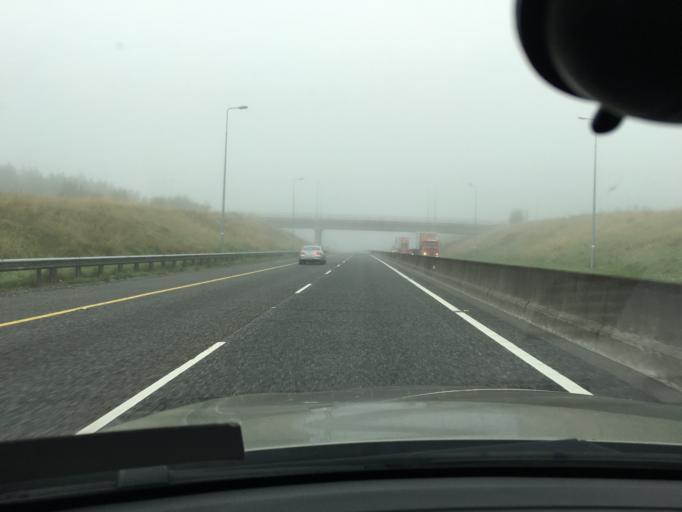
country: IE
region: Leinster
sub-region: An Iarmhi
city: Rochfortbridge
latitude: 53.3886
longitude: -7.3602
